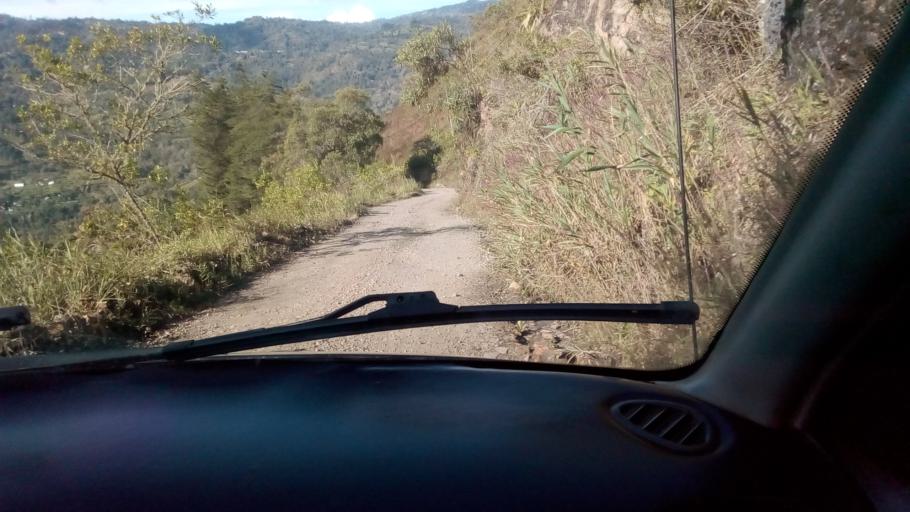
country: CO
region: Cundinamarca
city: Tenza
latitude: 5.0913
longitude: -73.4229
